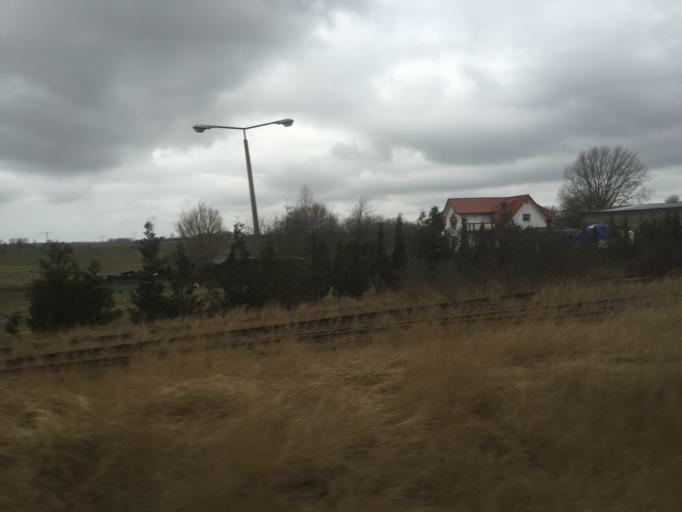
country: DE
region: Mecklenburg-Vorpommern
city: Bergen auf Ruegen
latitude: 54.4161
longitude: 13.4100
